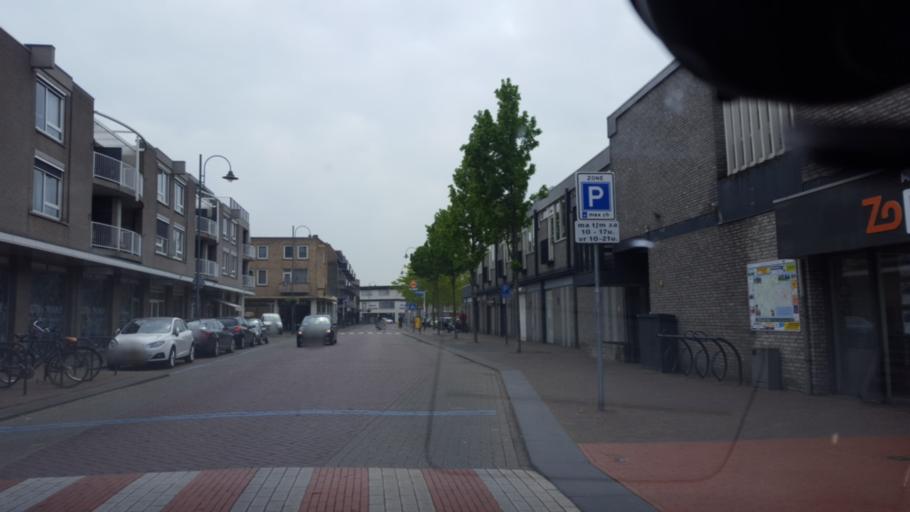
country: NL
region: North Brabant
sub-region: Gemeente Veghel
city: Veghel
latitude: 51.6173
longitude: 5.5462
